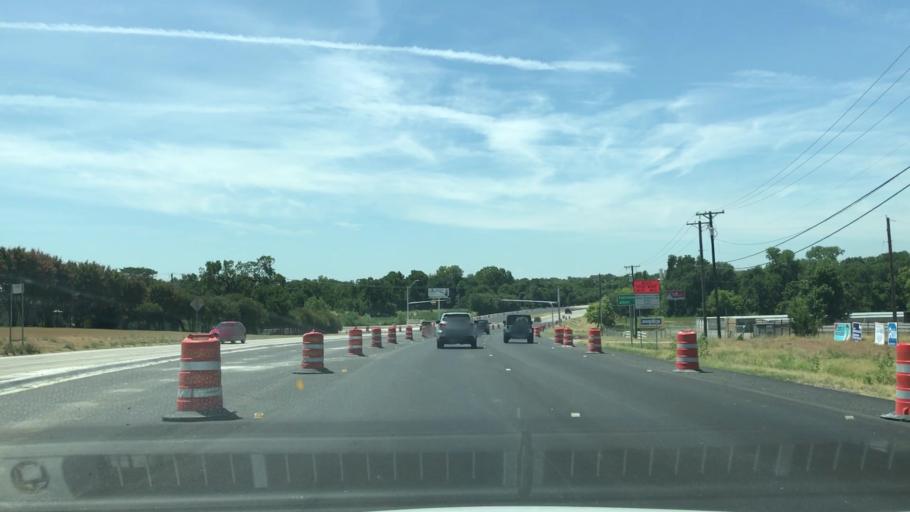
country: US
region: Texas
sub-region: Collin County
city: McKinney
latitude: 33.1778
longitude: -96.6194
